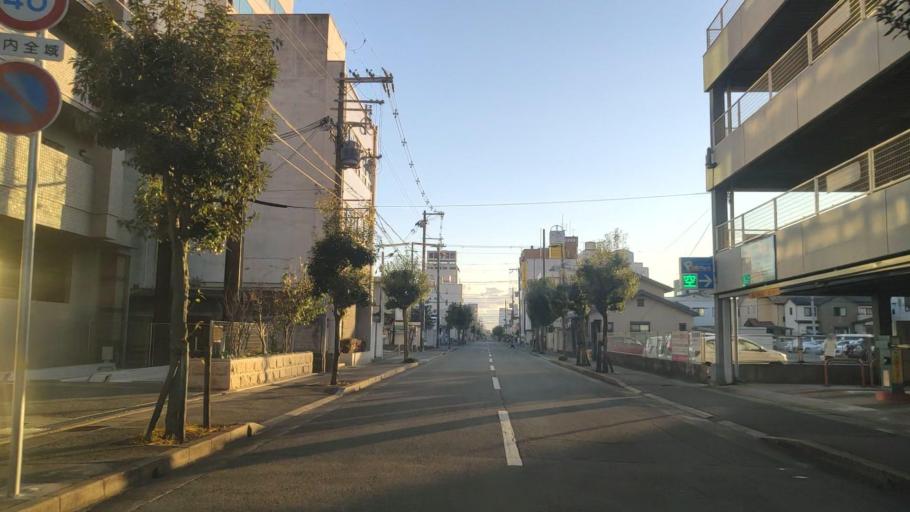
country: JP
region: Hyogo
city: Himeji
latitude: 34.8263
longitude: 134.6858
